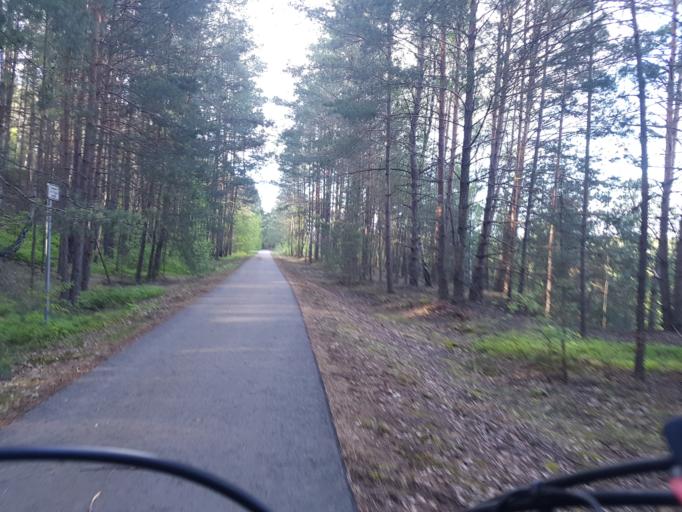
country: DE
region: Brandenburg
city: Trobitz
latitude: 51.5730
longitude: 13.4411
